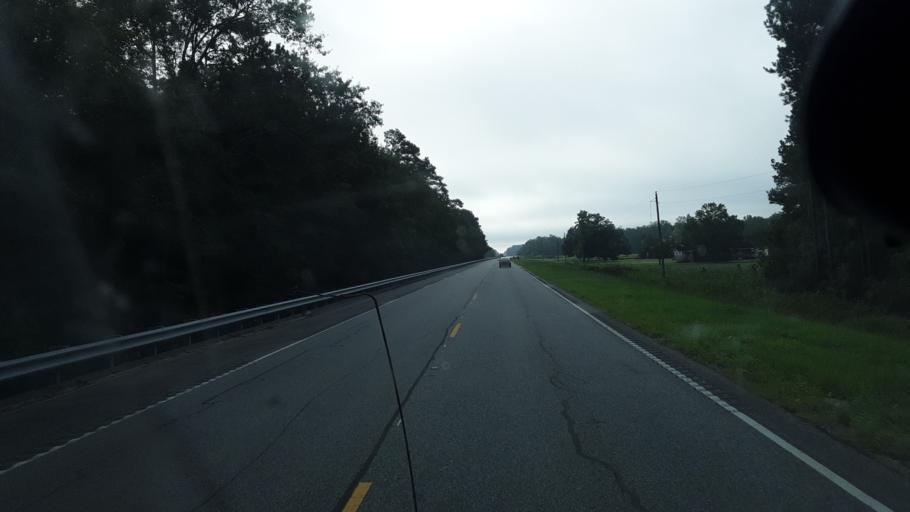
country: US
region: South Carolina
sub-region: Florence County
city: Johnsonville
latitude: 33.8532
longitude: -79.3024
